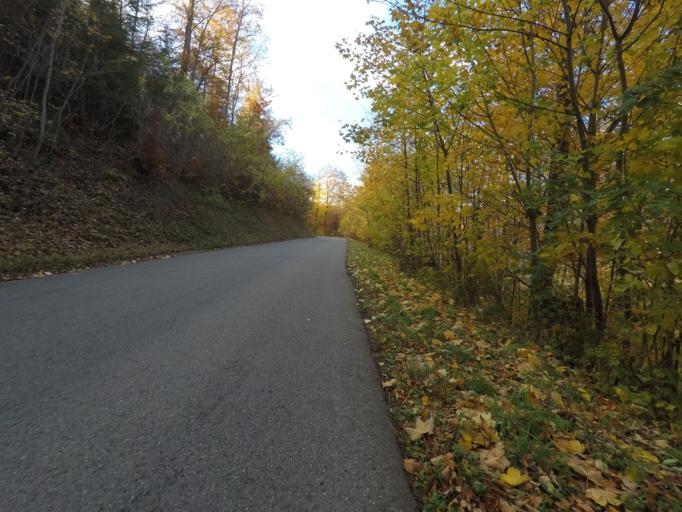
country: DE
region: Baden-Wuerttemberg
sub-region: Tuebingen Region
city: Pfullingen
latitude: 48.4249
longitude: 9.2465
